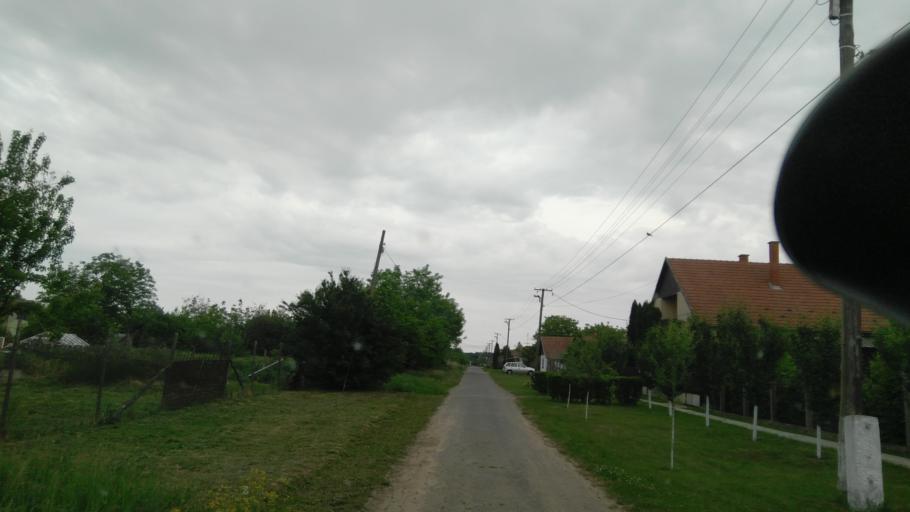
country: HU
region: Bekes
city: Doboz
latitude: 46.7260
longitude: 21.2460
